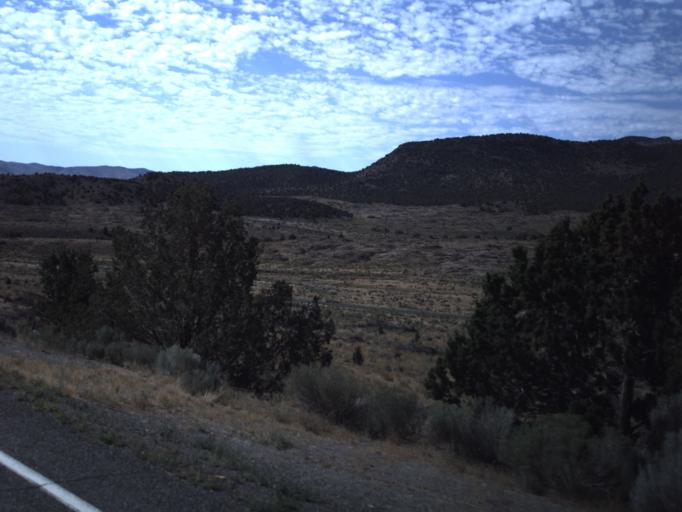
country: US
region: Utah
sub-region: Utah County
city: Genola
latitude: 39.9557
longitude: -112.0343
